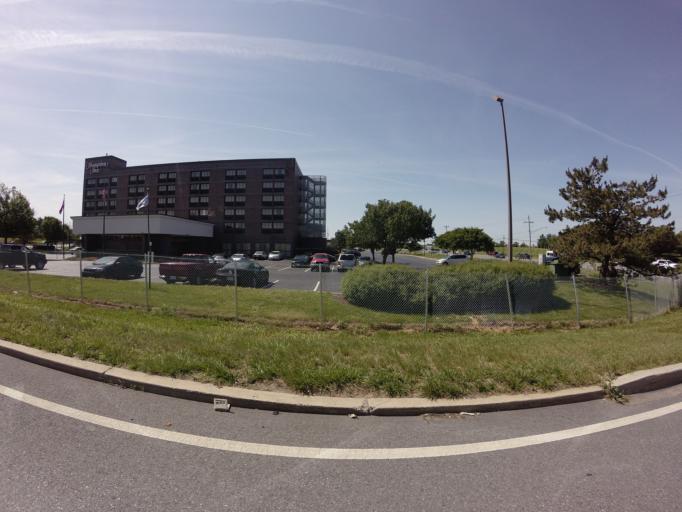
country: US
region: Maryland
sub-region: Frederick County
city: Ballenger Creek
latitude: 39.3794
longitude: -77.4088
